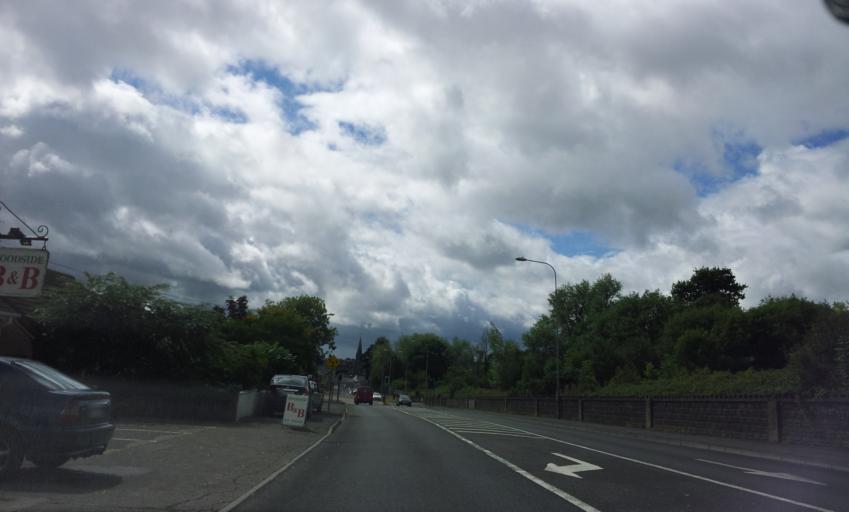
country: IE
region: Munster
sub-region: Waterford
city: Waterford
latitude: 52.2703
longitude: -7.0939
